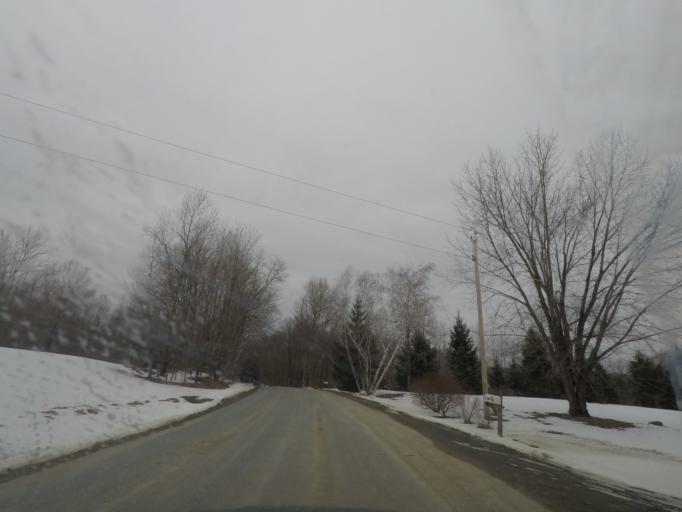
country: US
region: New York
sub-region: Rensselaer County
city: Averill Park
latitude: 42.5574
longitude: -73.4121
